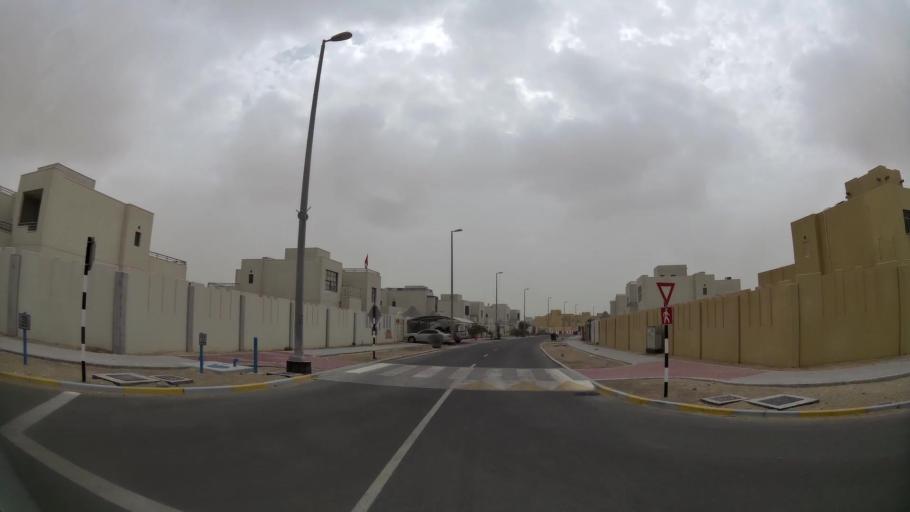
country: AE
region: Abu Dhabi
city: Abu Dhabi
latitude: 24.4473
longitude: 54.7307
